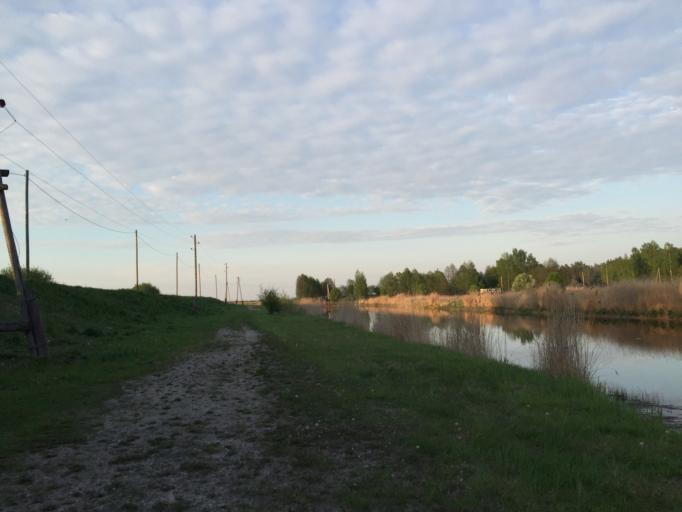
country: LV
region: Jurmala
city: Jurmala
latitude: 56.9076
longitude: 23.7396
